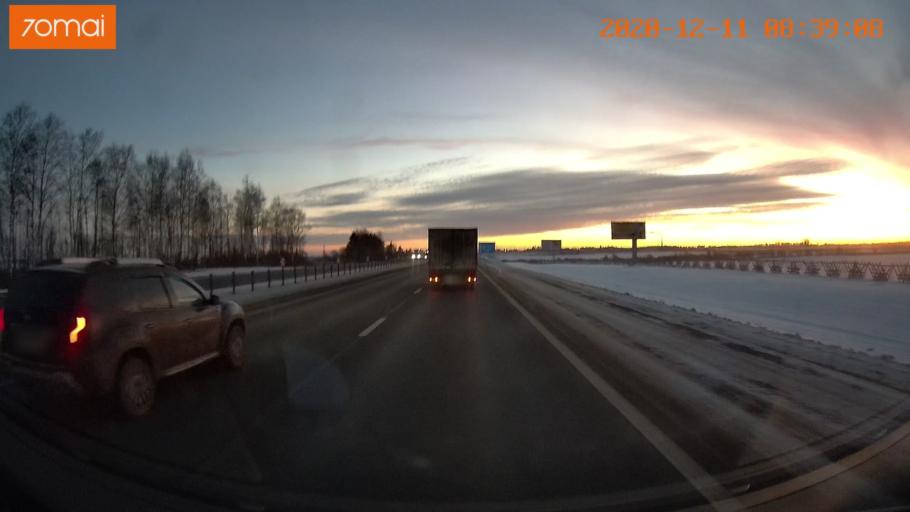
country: RU
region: Vologda
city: Molochnoye
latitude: 59.2130
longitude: 39.7465
